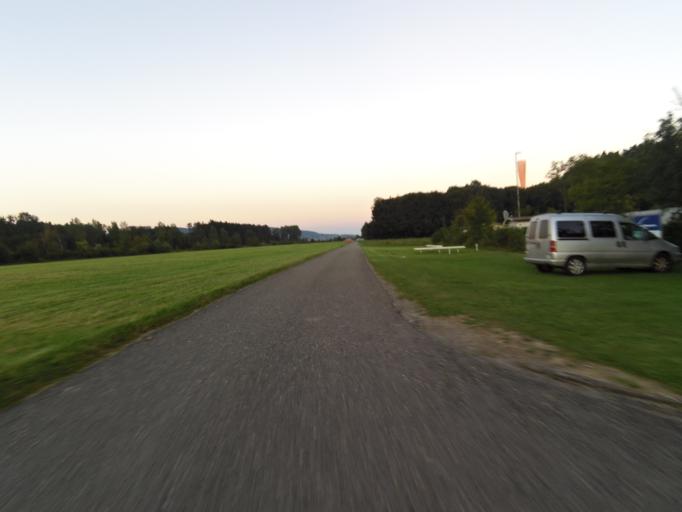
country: CH
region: Thurgau
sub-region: Weinfelden District
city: Maerstetten-Dorf
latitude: 47.5737
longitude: 9.0497
